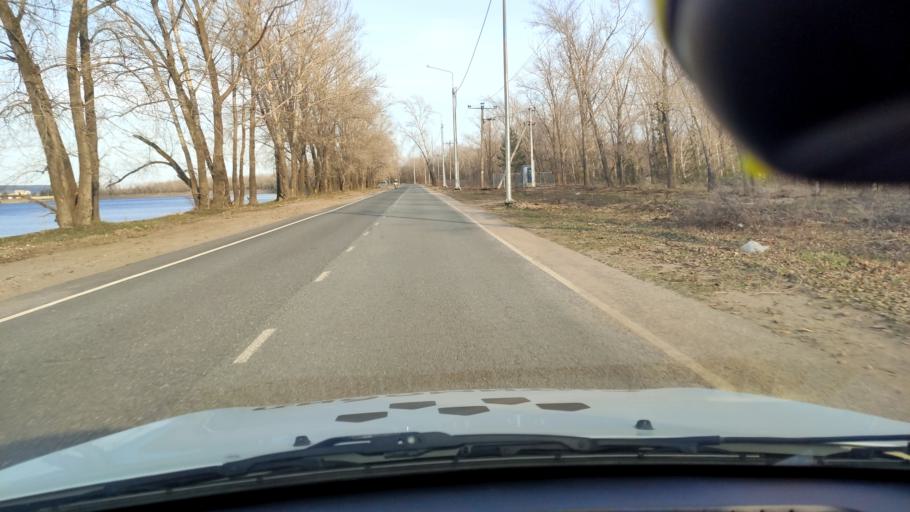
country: RU
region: Samara
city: Zhigulevsk
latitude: 53.4565
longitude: 49.5462
